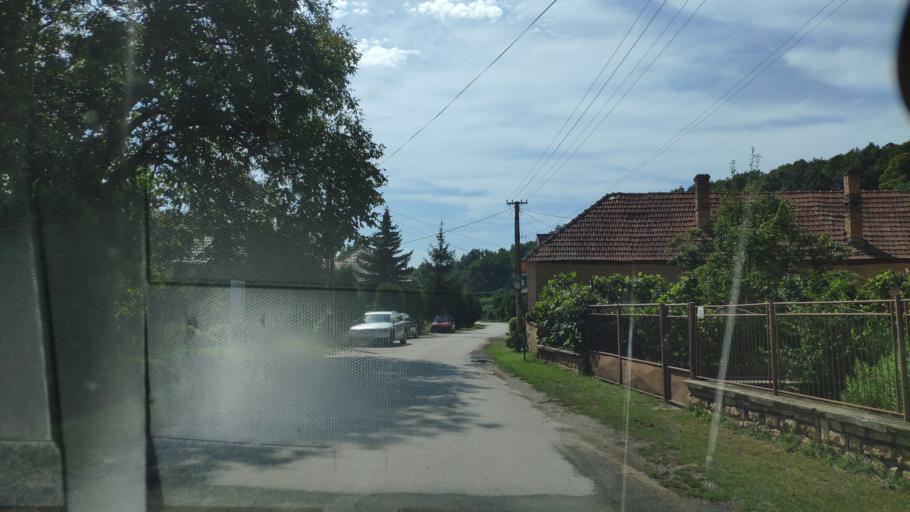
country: SK
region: Kosicky
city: Roznava
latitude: 48.5317
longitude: 20.4145
